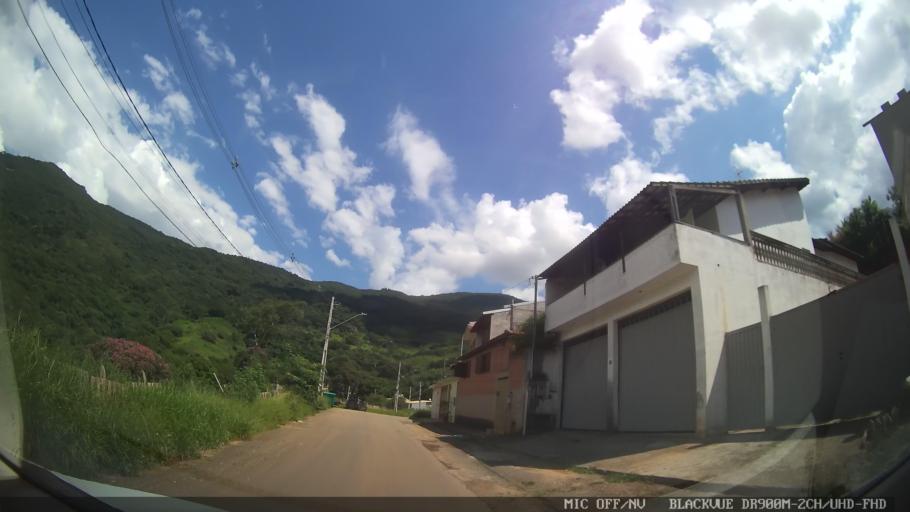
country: BR
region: Minas Gerais
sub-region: Extrema
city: Extrema
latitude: -22.8662
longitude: -46.3268
